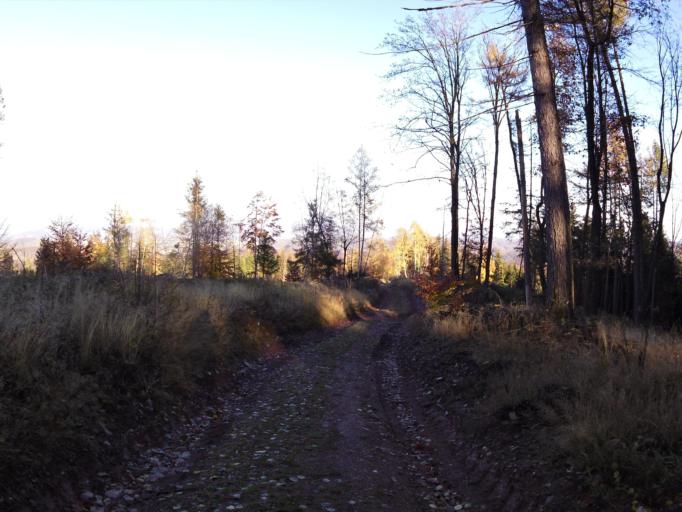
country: DE
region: Thuringia
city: Ruhla
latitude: 50.9064
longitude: 10.3639
